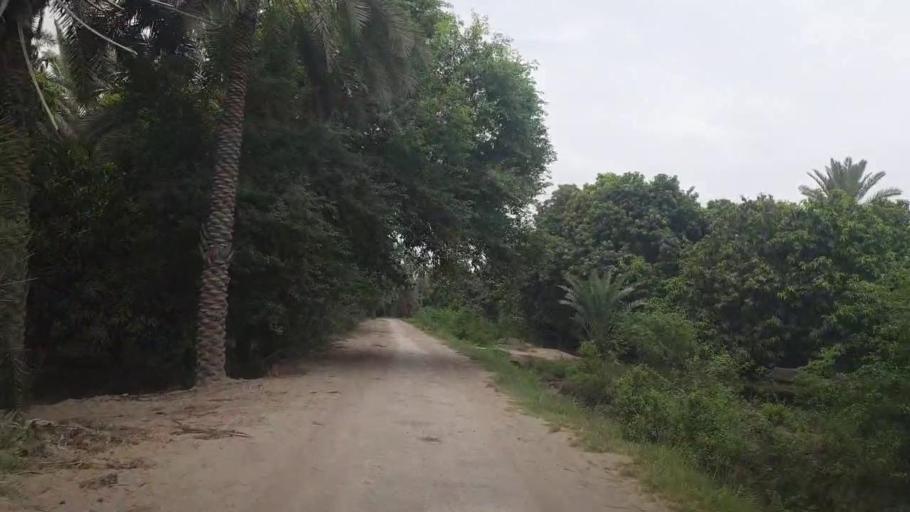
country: PK
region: Sindh
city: Khairpur
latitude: 27.5858
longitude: 68.7137
